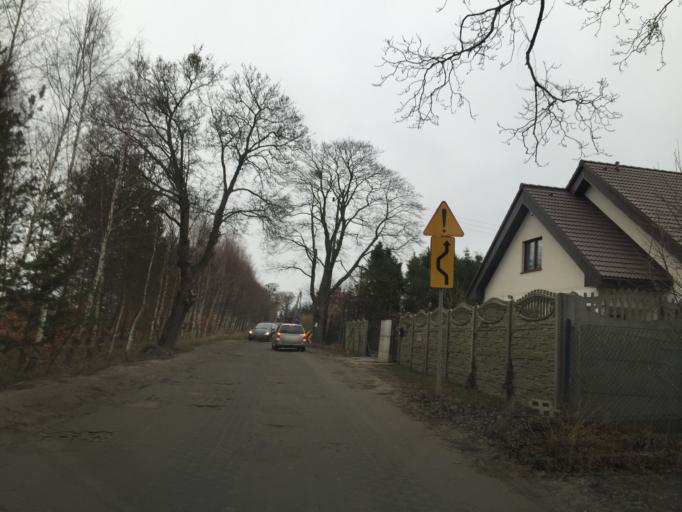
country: PL
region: Pomeranian Voivodeship
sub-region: Powiat kartuski
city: Banino
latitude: 54.4094
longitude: 18.4432
